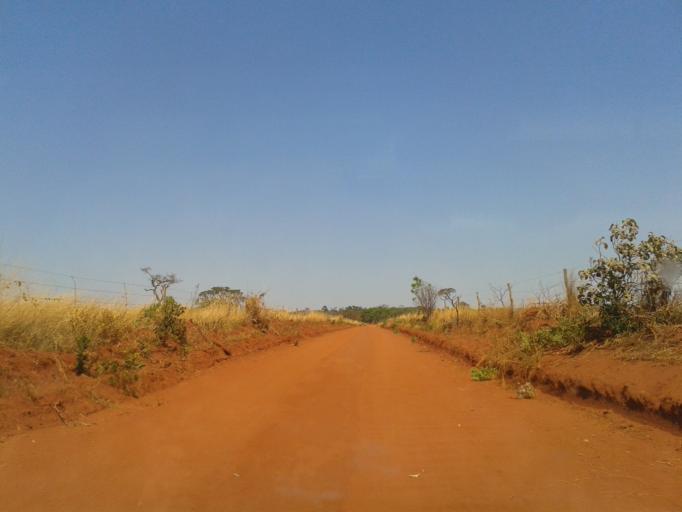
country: BR
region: Minas Gerais
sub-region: Ituiutaba
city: Ituiutaba
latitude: -19.0684
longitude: -49.3392
